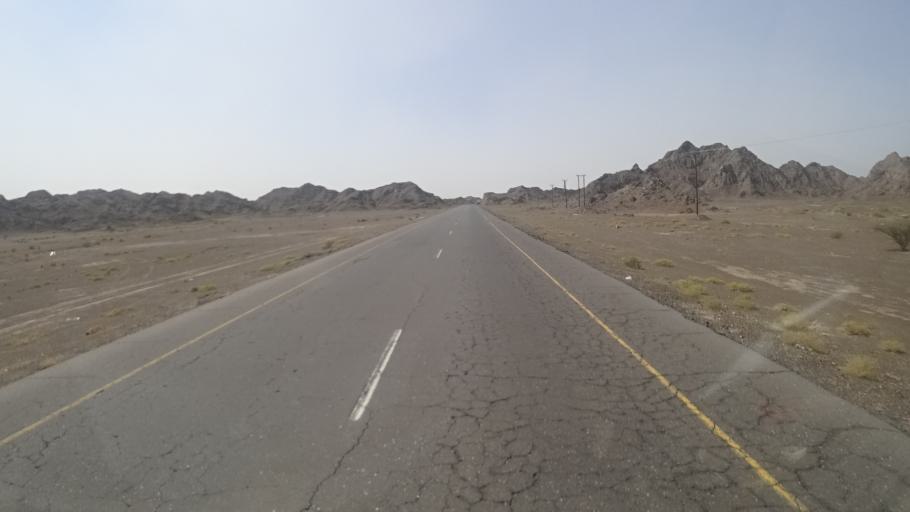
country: OM
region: Ash Sharqiyah
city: Ibra'
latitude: 22.6206
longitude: 58.3137
